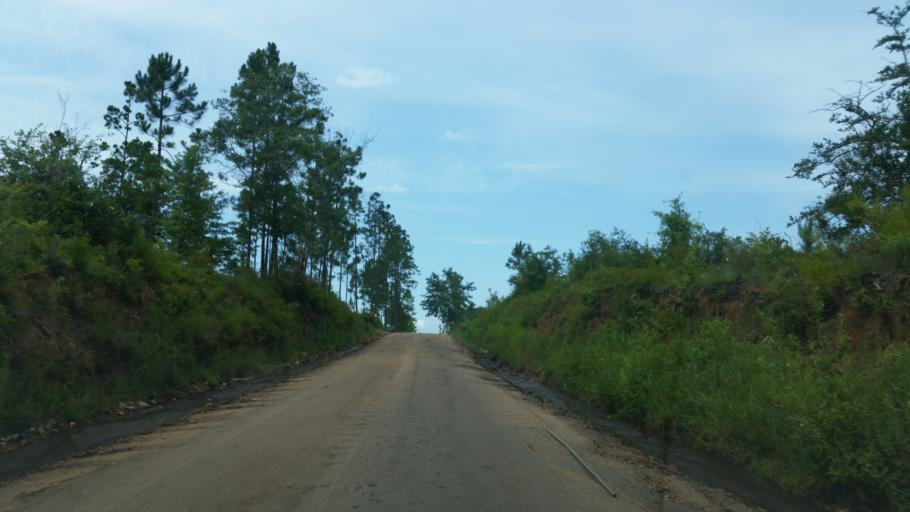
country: US
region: Florida
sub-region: Escambia County
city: Cantonment
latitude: 30.6160
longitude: -87.3875
